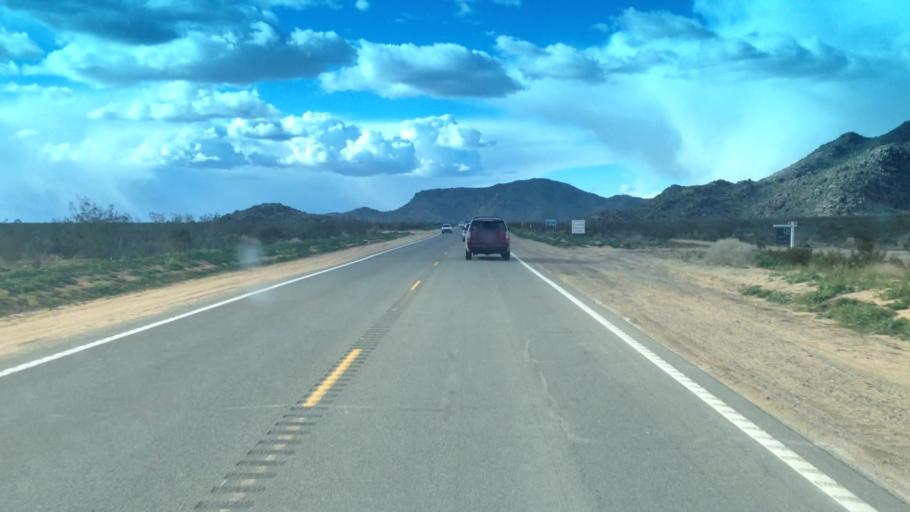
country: US
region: California
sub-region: San Bernardino County
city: Lucerne Valley
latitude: 34.4584
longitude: -117.0755
